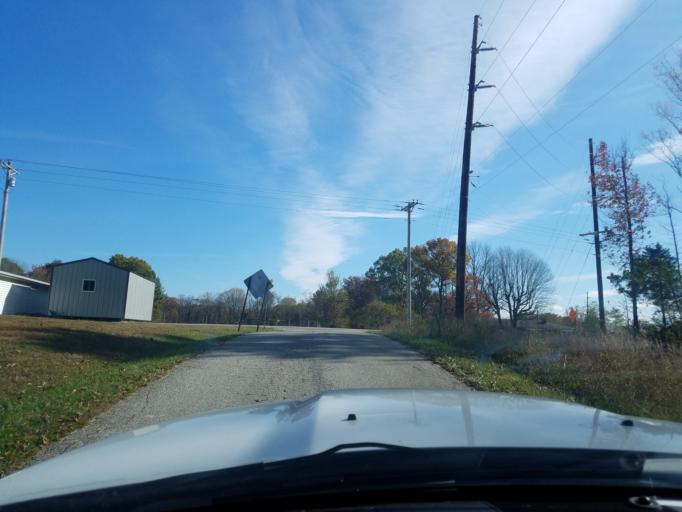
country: US
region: Indiana
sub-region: Jennings County
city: North Vernon
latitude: 39.0219
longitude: -85.6157
